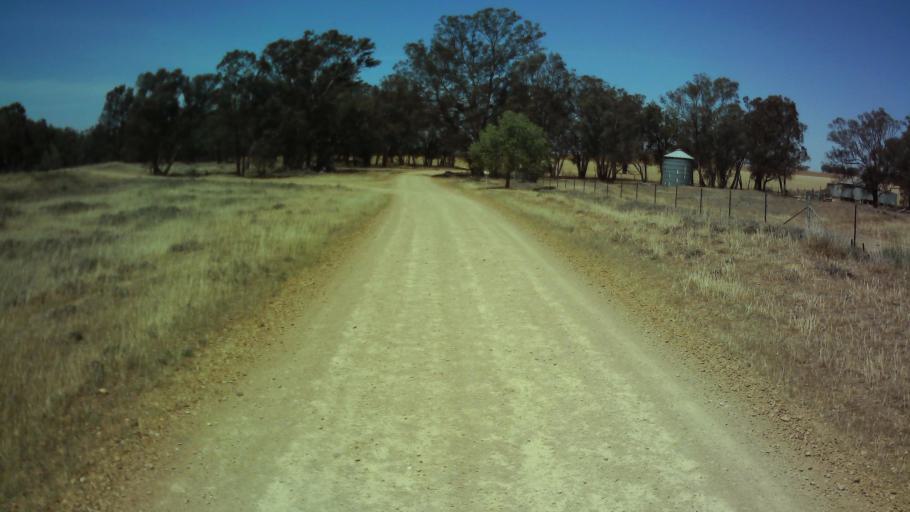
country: AU
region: New South Wales
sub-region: Weddin
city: Grenfell
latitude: -33.9234
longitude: 148.1902
